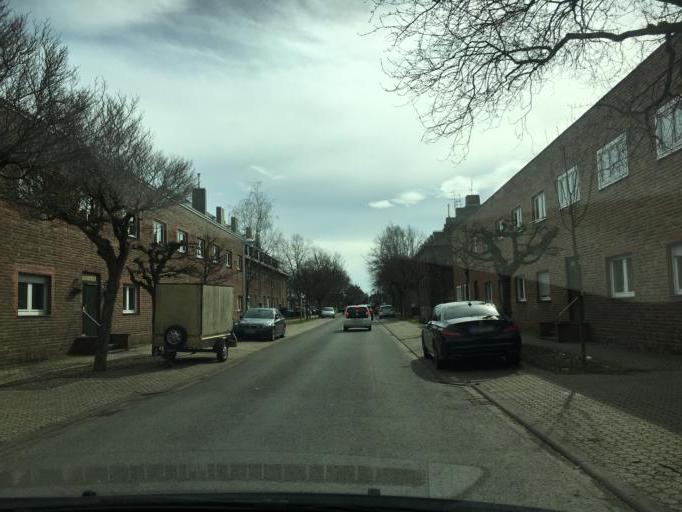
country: DE
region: North Rhine-Westphalia
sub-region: Regierungsbezirk Koln
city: Dueren
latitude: 50.8146
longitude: 6.4963
